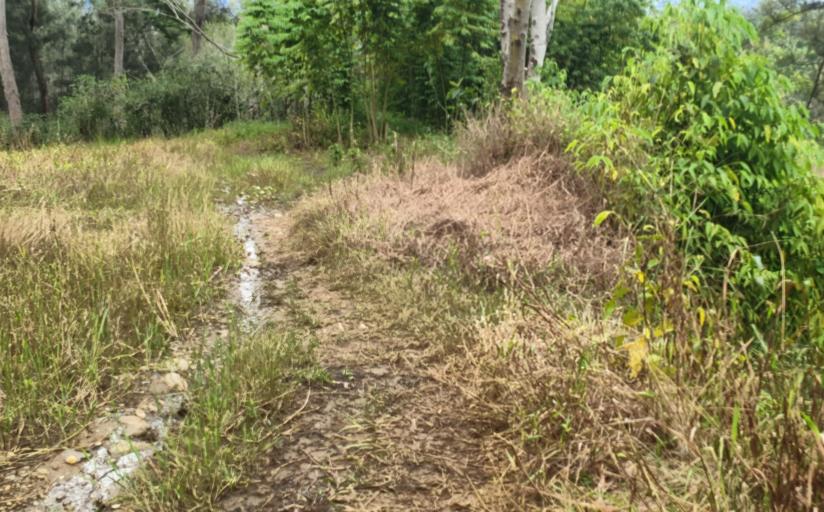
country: PG
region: Jiwaka
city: Minj
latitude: -5.9145
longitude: 144.8250
